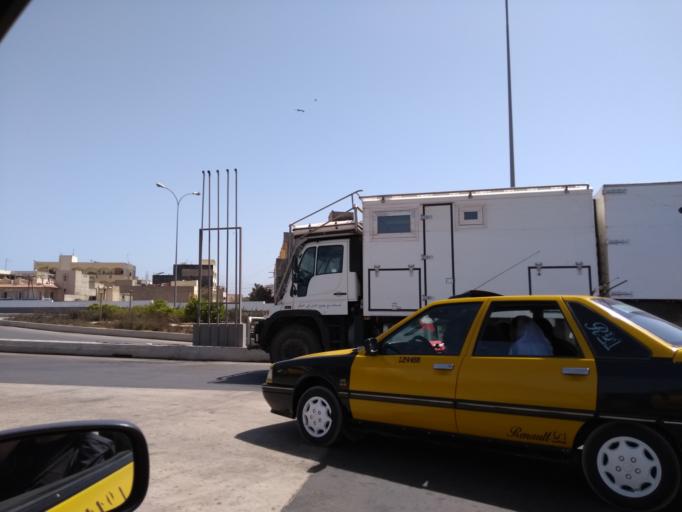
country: SN
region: Dakar
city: Pikine
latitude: 14.7452
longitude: -17.4194
